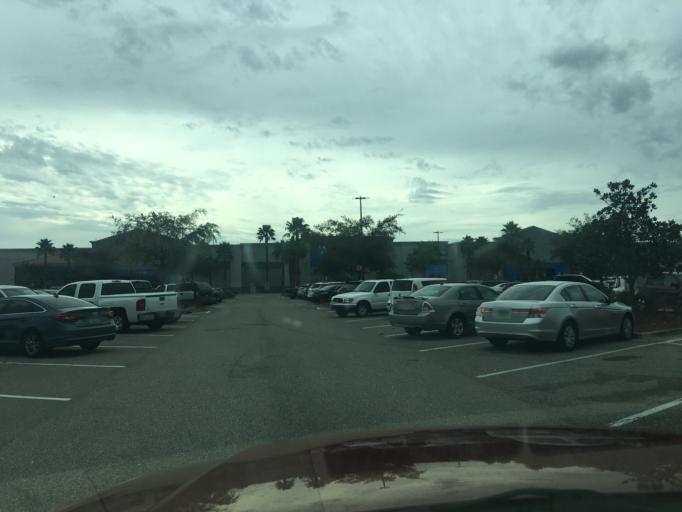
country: US
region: Florida
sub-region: Hillsborough County
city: Gibsonton
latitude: 27.8488
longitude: -82.3540
